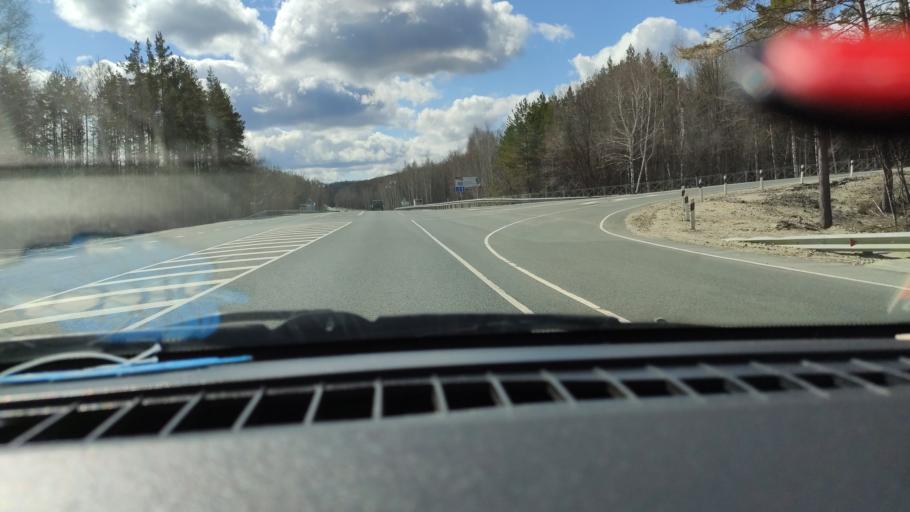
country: RU
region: Saratov
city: Khvalynsk
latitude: 52.5110
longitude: 48.0160
